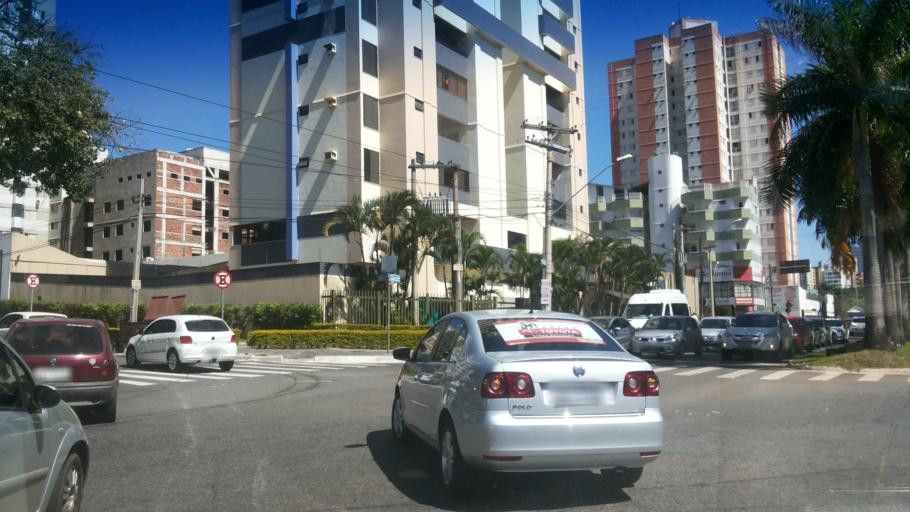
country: BR
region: Goias
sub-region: Goiania
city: Goiania
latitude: -16.7099
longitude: -49.2588
